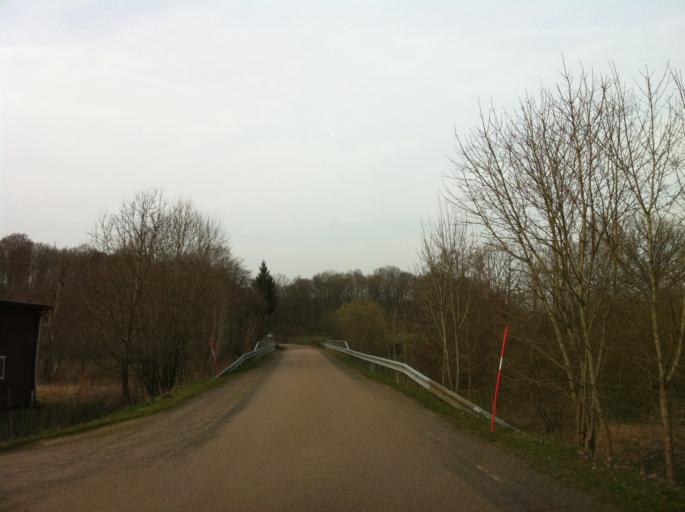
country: SE
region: Skane
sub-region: Eslovs Kommun
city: Stehag
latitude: 56.0172
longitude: 13.3783
